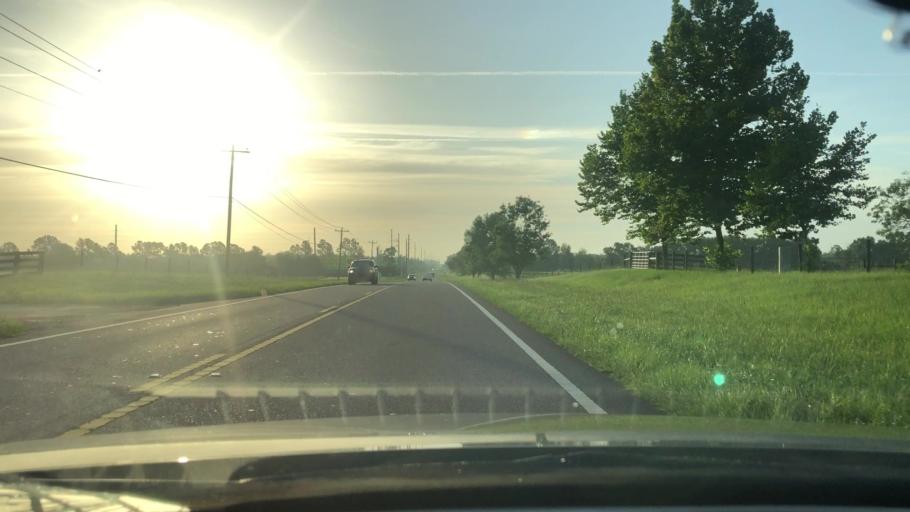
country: US
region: Florida
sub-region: Marion County
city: Belleview
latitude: 29.0261
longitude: -82.2069
